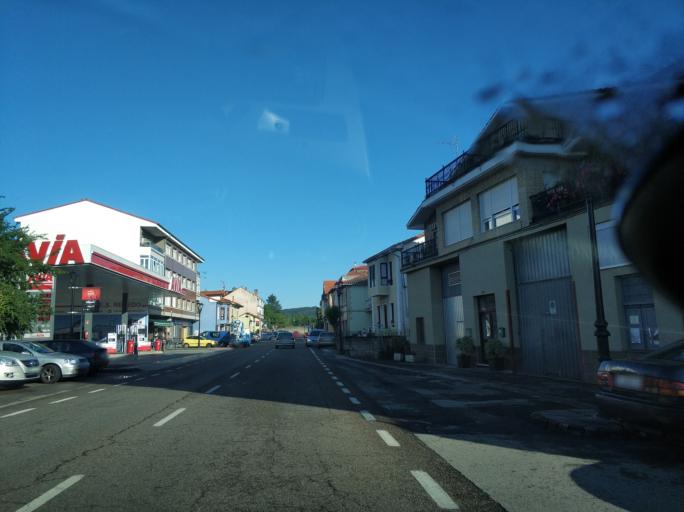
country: ES
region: Cantabria
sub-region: Provincia de Cantabria
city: Puente Viesgo
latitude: 43.3552
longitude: -3.9548
